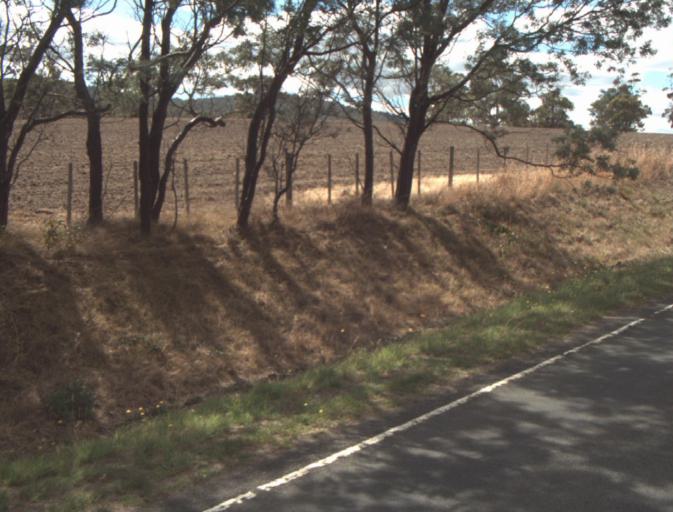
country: AU
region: Tasmania
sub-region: Launceston
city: Mayfield
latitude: -41.3353
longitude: 147.0790
